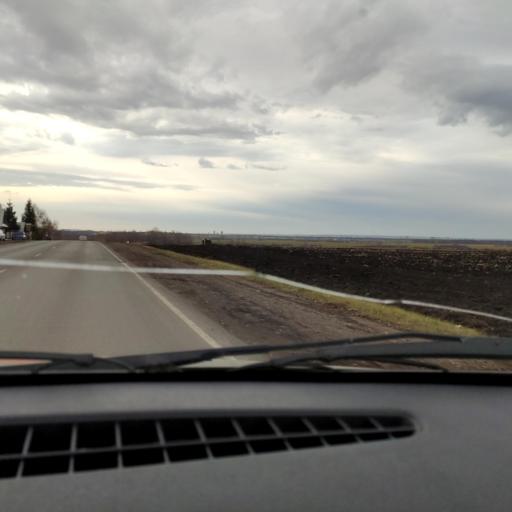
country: RU
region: Bashkortostan
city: Ufa
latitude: 54.8217
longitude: 55.9866
